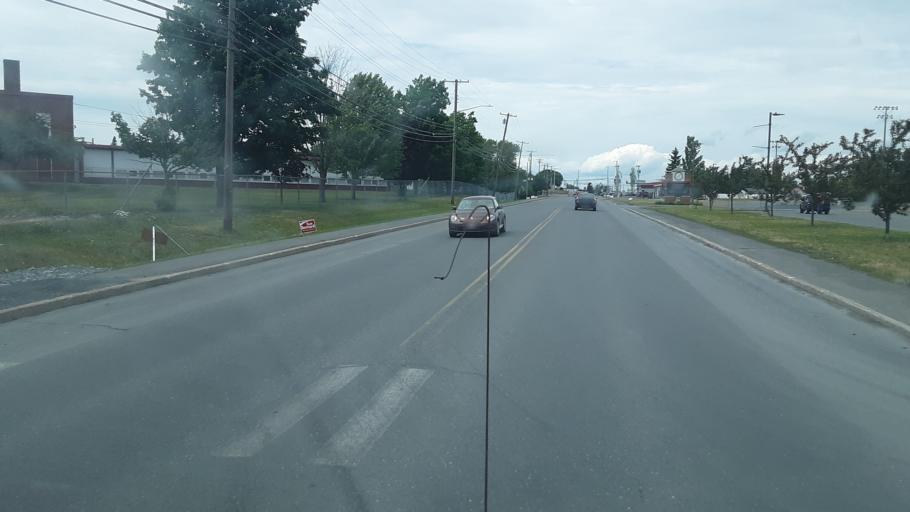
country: US
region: Maine
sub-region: Aroostook County
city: Caribou
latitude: 46.8641
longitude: -68.0049
